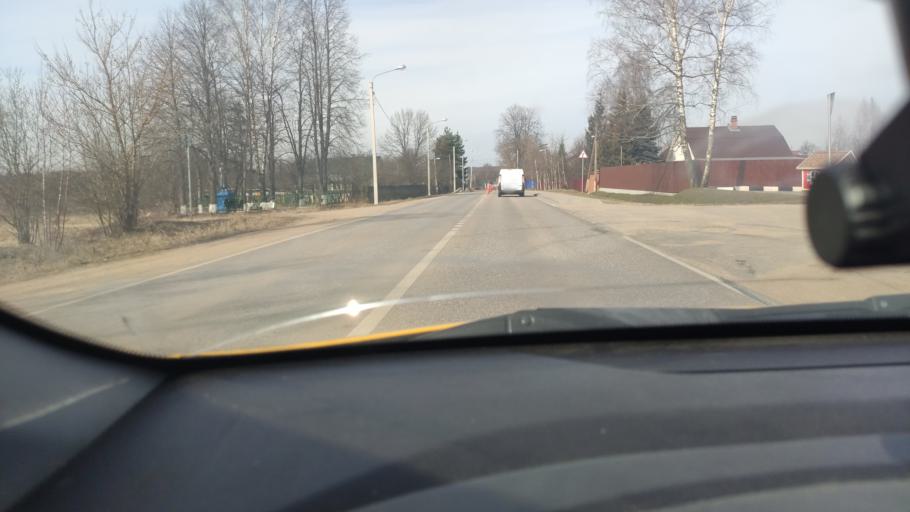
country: RU
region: Moskovskaya
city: Ruza
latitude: 55.7348
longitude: 36.1415
